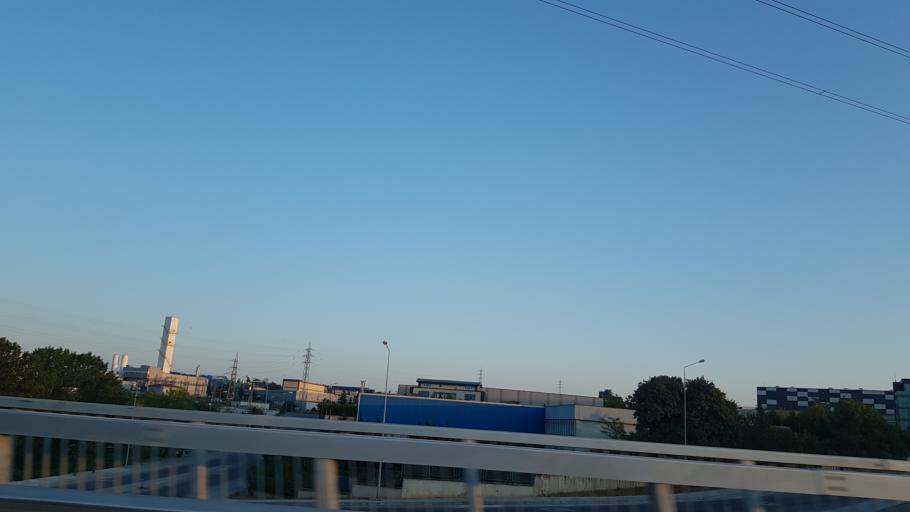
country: TR
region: Kocaeli
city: Tavsanli
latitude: 40.8002
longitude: 29.5176
